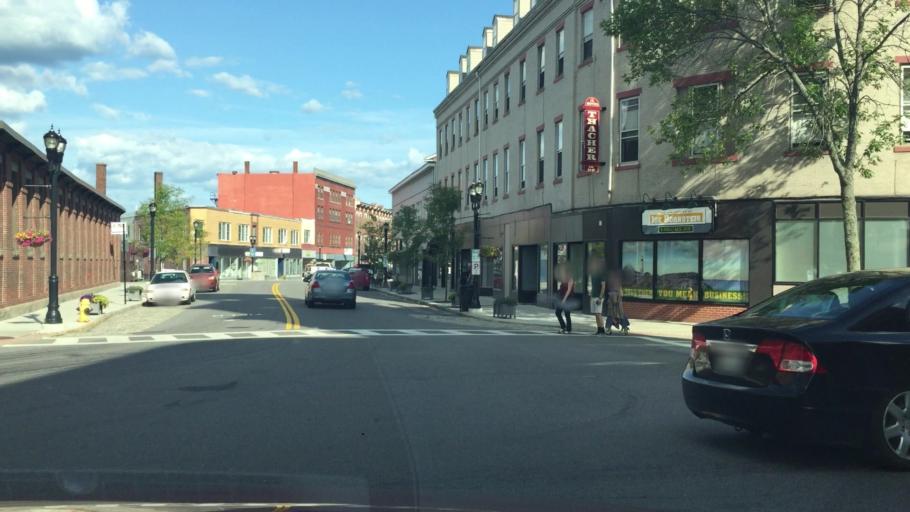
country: US
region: Maine
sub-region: York County
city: Biddeford
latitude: 43.4935
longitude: -70.4561
